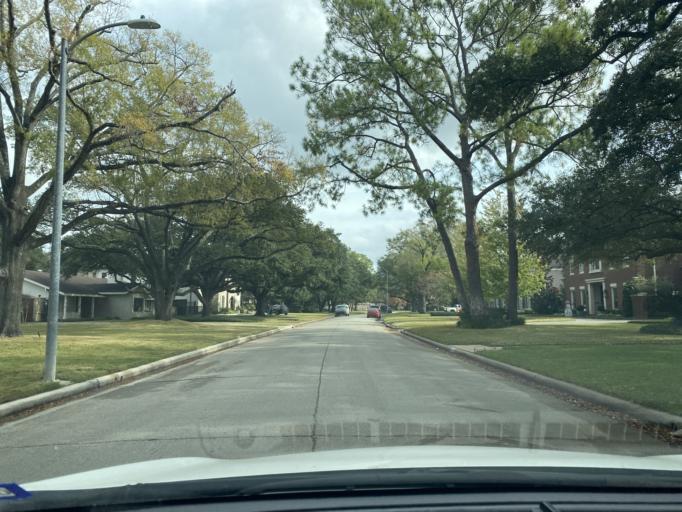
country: US
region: Texas
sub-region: Harris County
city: Hunters Creek Village
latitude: 29.7547
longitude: -95.4759
